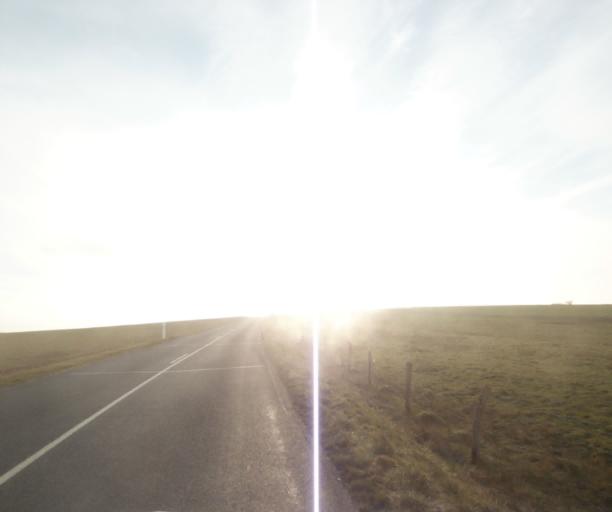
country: FR
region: Champagne-Ardenne
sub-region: Departement de la Marne
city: Sermaize-les-Bains
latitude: 48.7331
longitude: 4.9293
